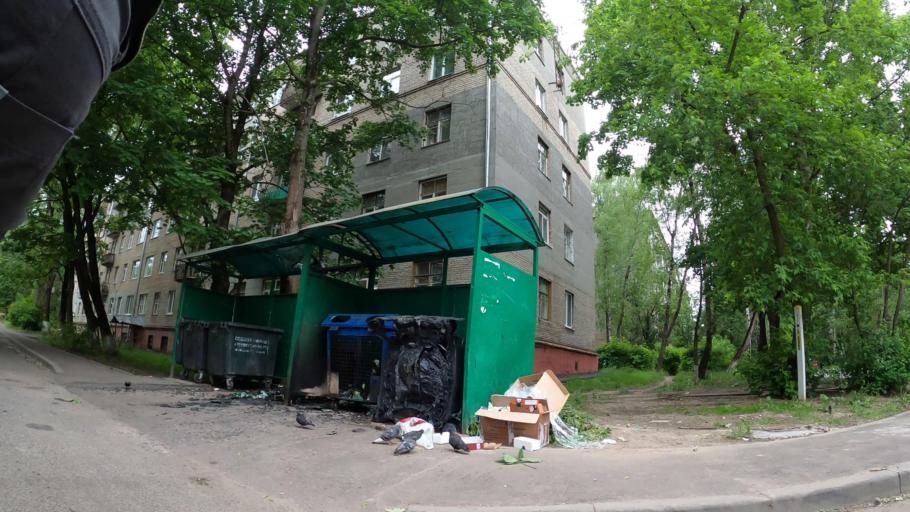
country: RU
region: Moskovskaya
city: Yubileyny
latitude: 55.9435
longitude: 37.8411
